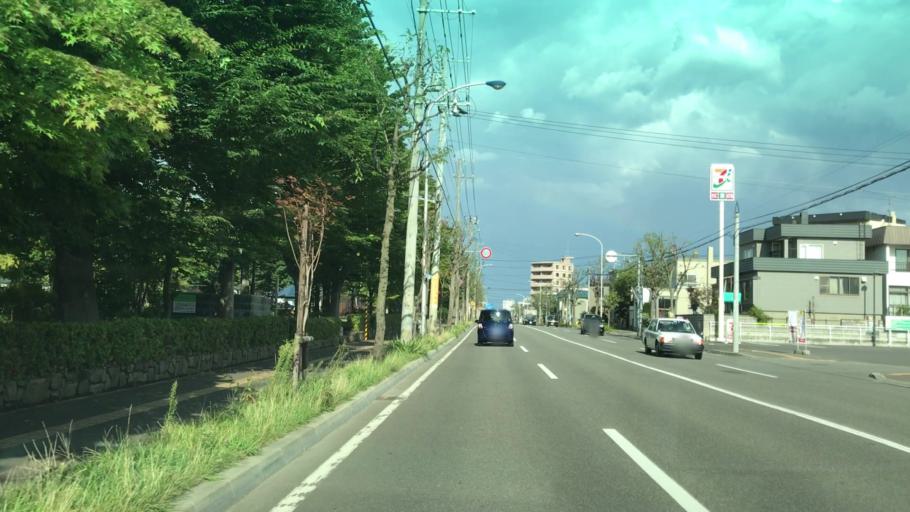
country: JP
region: Hokkaido
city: Sapporo
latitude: 43.0848
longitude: 141.2984
